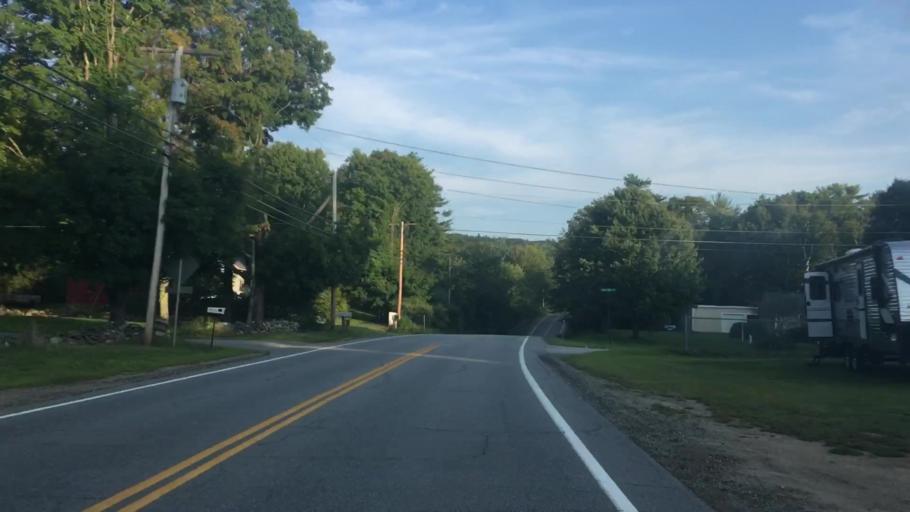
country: US
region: New Hampshire
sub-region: Belknap County
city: Gilmanton
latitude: 43.4693
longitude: -71.4235
